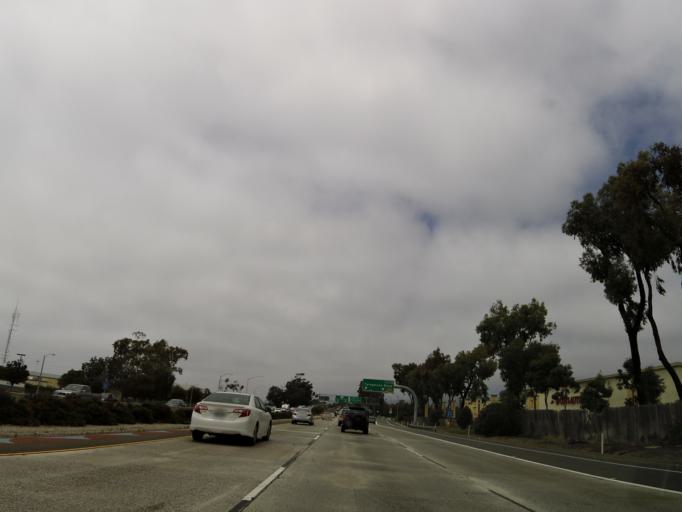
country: US
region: California
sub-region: Ventura County
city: El Rio
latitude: 34.2605
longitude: -119.2269
